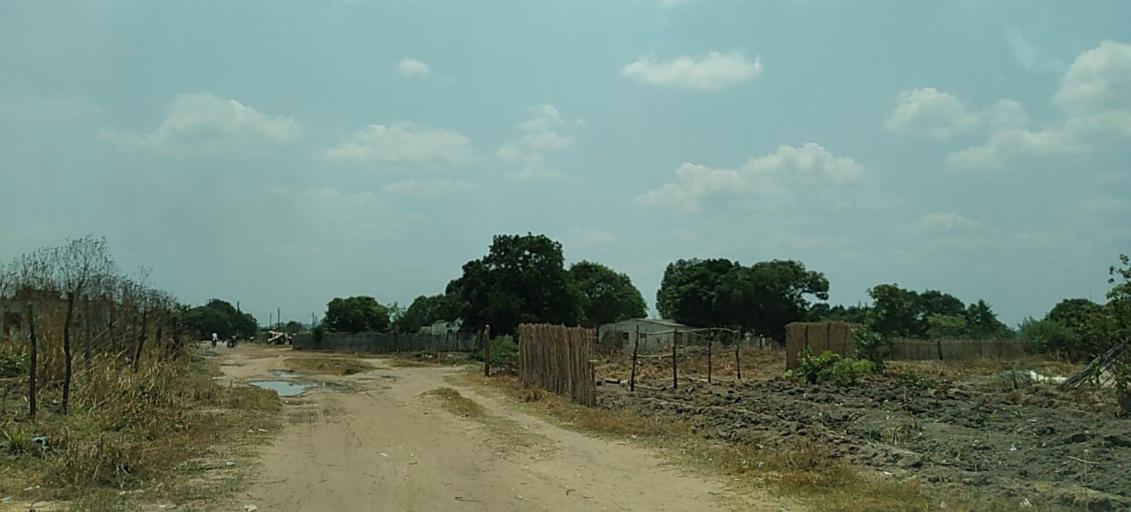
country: ZM
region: Copperbelt
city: Luanshya
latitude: -13.1006
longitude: 28.3037
